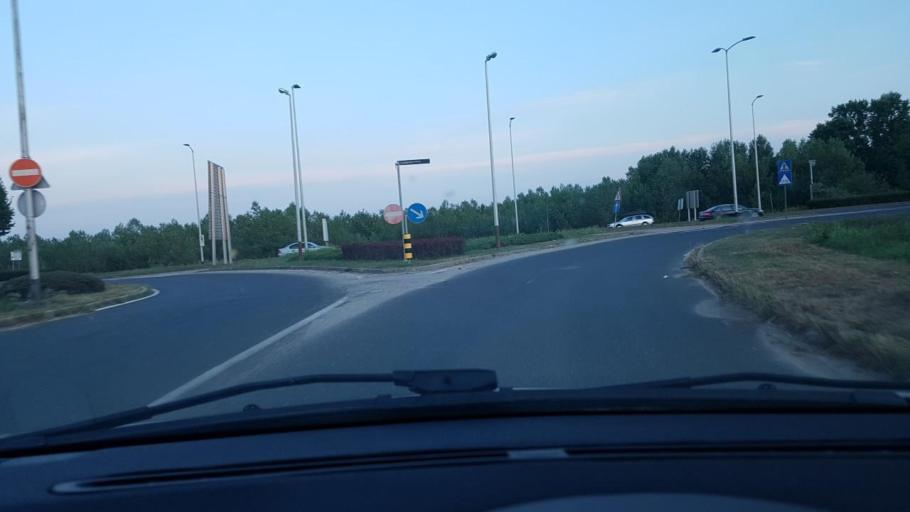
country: HR
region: Grad Zagreb
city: Jezdovec
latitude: 45.7943
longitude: 15.8570
